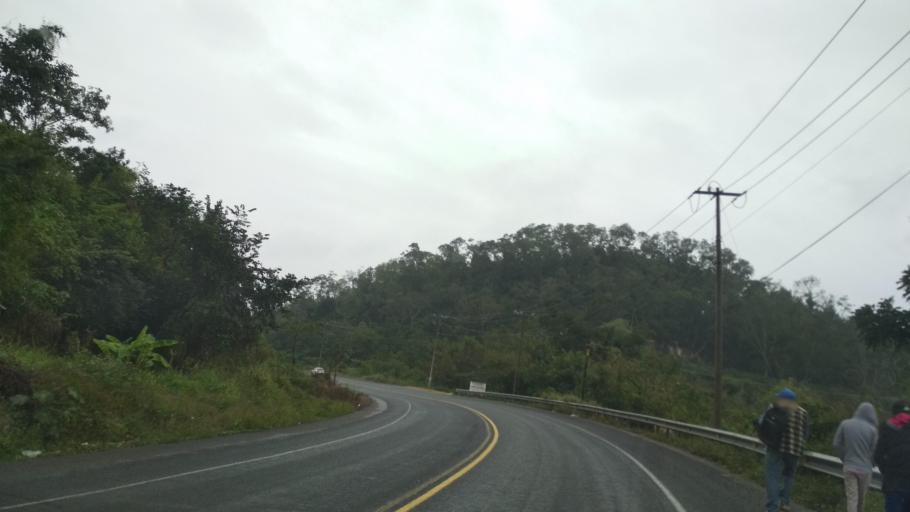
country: MX
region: Veracruz
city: Papantla de Olarte
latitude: 20.4666
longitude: -97.3150
